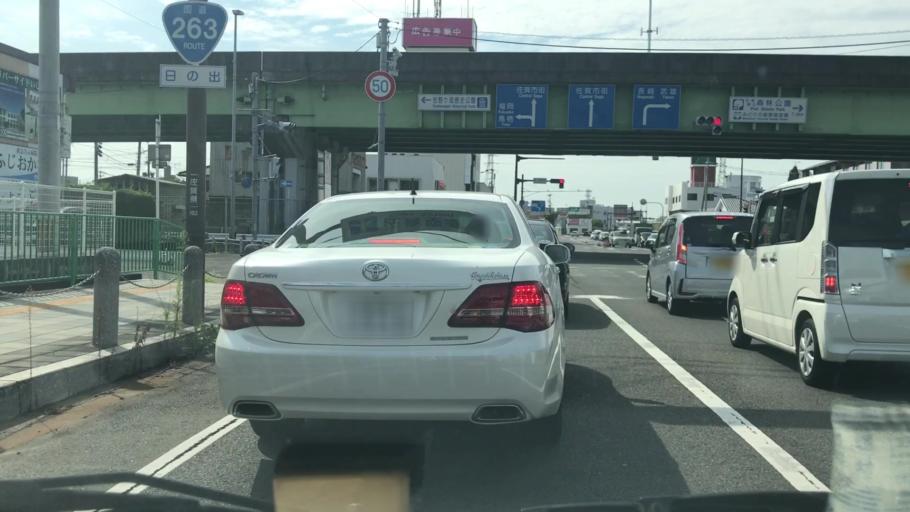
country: JP
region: Saga Prefecture
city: Saga-shi
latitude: 33.2747
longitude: 130.2937
